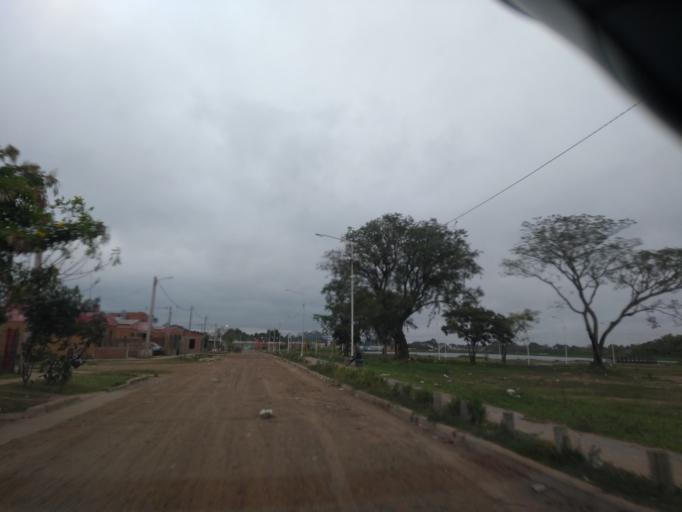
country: AR
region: Chaco
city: Resistencia
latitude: -27.4586
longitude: -58.9653
